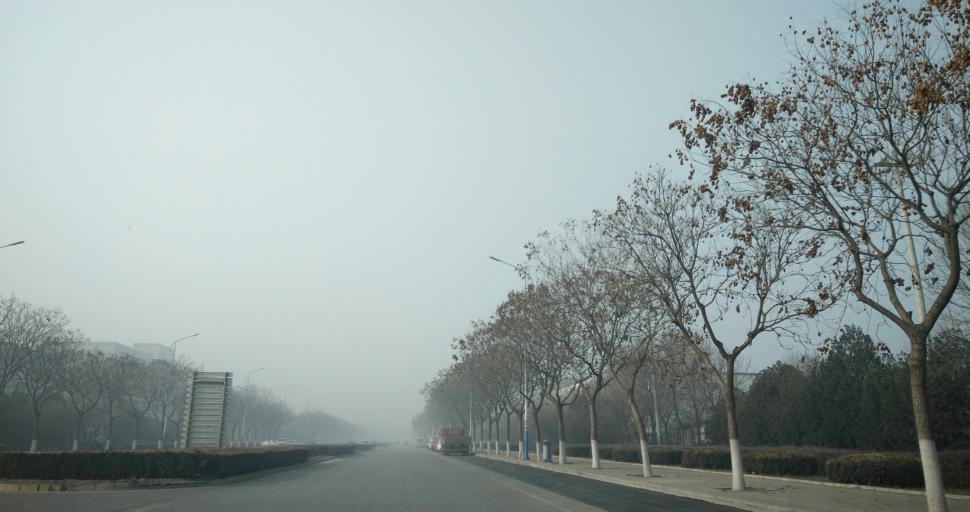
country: CN
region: Beijing
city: Yinghai
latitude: 39.7085
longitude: 116.4130
